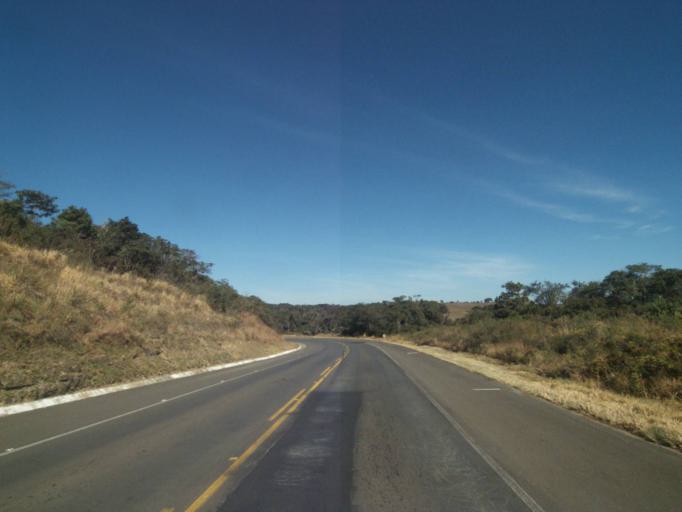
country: BR
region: Parana
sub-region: Tibagi
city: Tibagi
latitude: -24.7858
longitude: -50.4694
